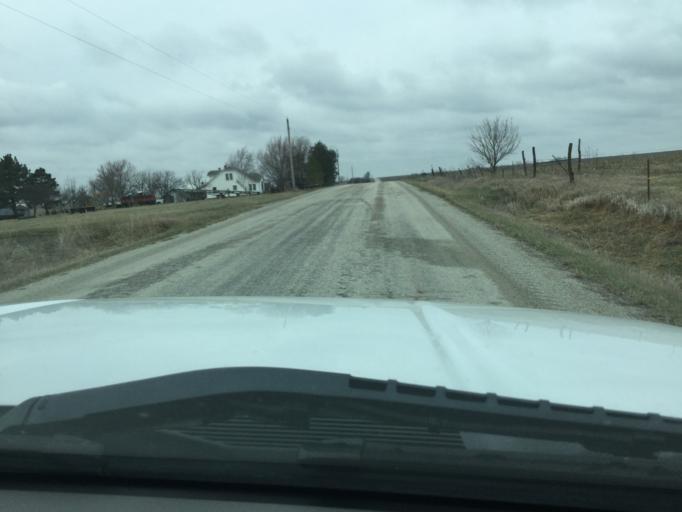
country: US
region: Kansas
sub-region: Nemaha County
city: Sabetha
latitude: 39.7980
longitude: -95.7611
